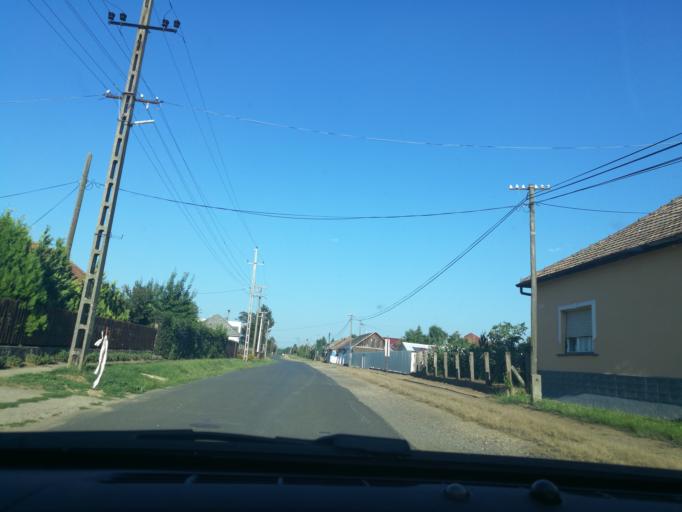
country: HU
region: Szabolcs-Szatmar-Bereg
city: Tiszabercel
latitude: 48.1692
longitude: 21.5628
